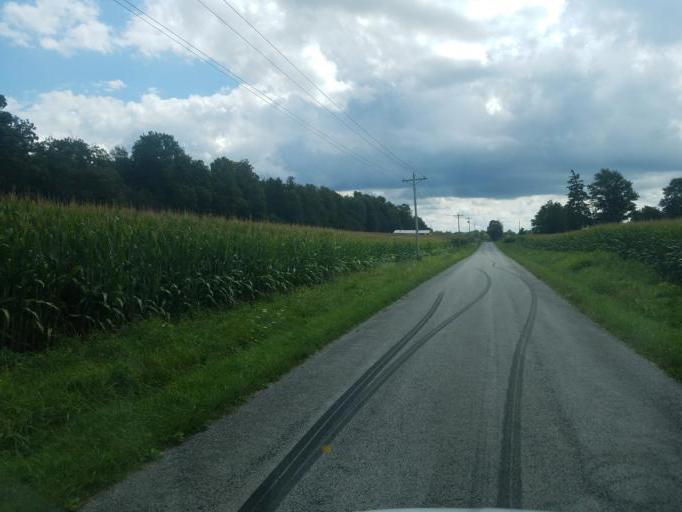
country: US
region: Ohio
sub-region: Huron County
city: Plymouth
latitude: 41.0880
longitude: -82.6296
